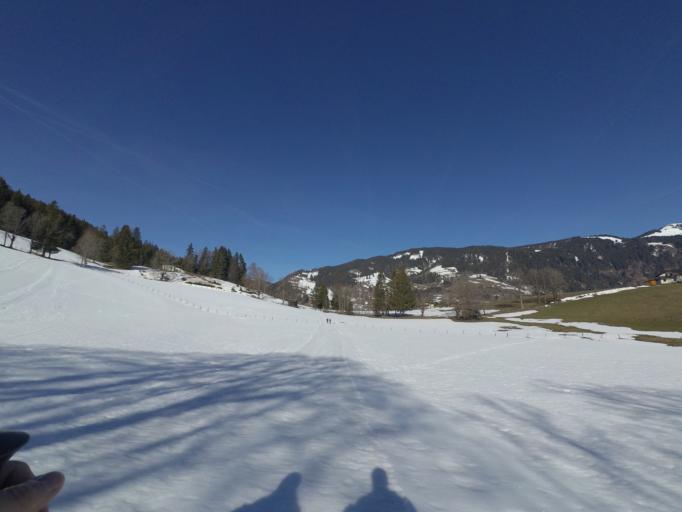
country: AT
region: Salzburg
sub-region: Politischer Bezirk Sankt Johann im Pongau
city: Goldegg
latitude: 47.3151
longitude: 13.0749
